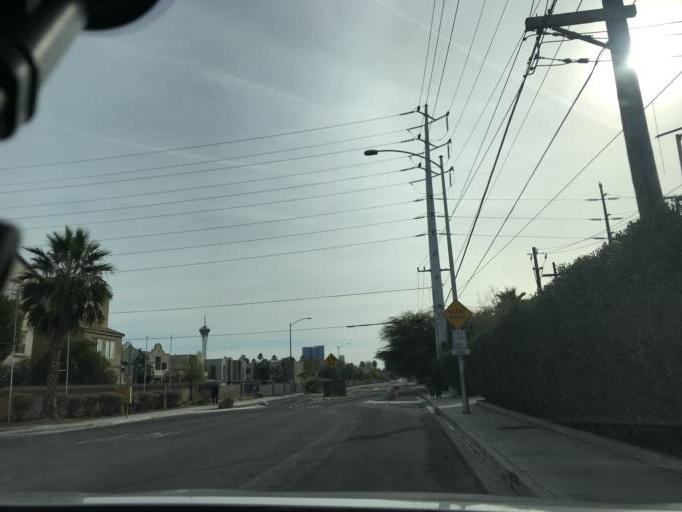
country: US
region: Nevada
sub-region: Clark County
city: Las Vegas
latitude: 36.1703
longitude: -115.1655
